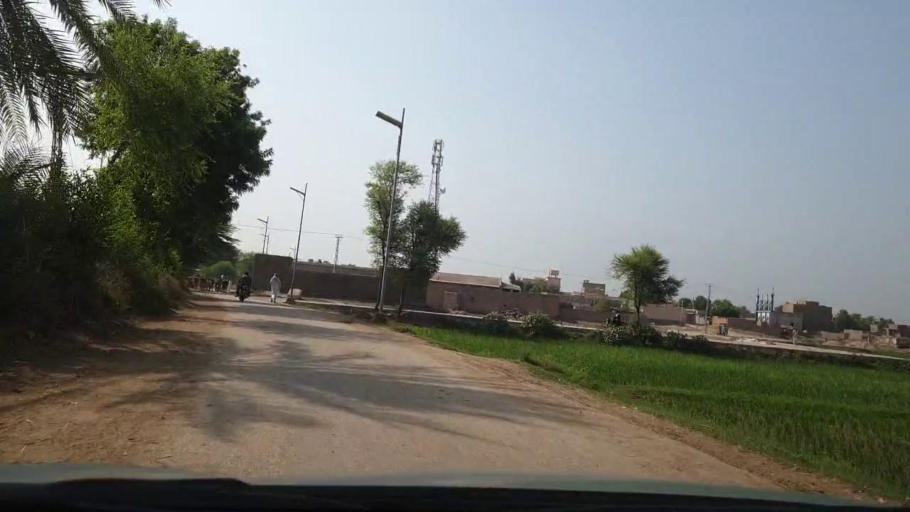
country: PK
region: Sindh
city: Larkana
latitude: 27.4613
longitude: 68.2297
